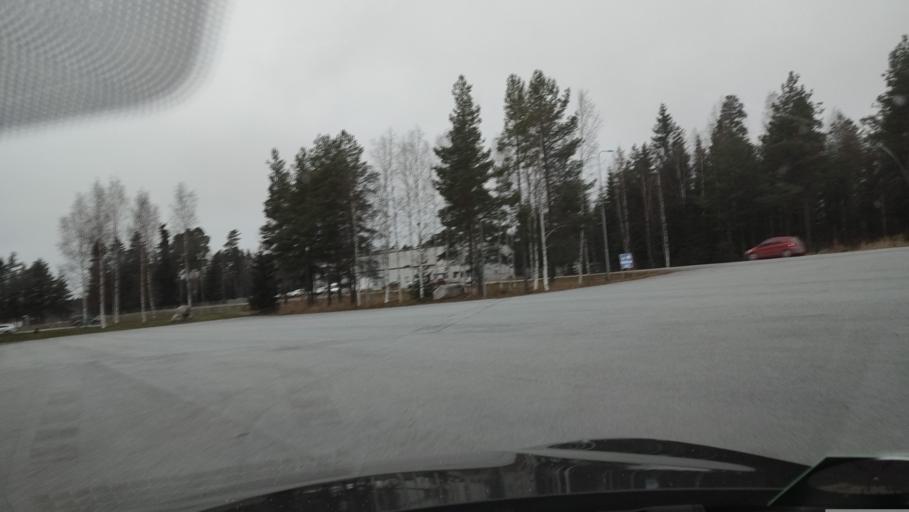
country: FI
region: Southern Ostrobothnia
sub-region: Suupohja
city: Kauhajoki
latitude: 62.4589
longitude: 22.1989
